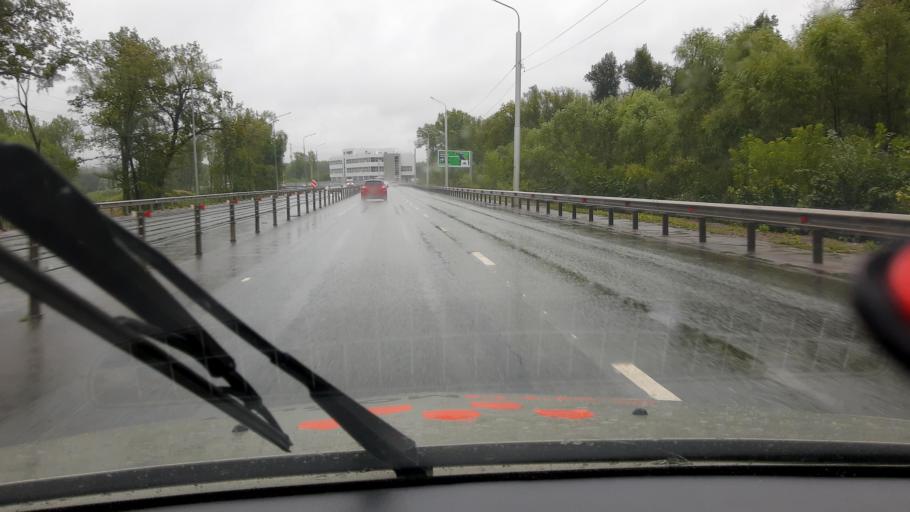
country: RU
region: Bashkortostan
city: Ufa
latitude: 54.6999
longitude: 55.8919
